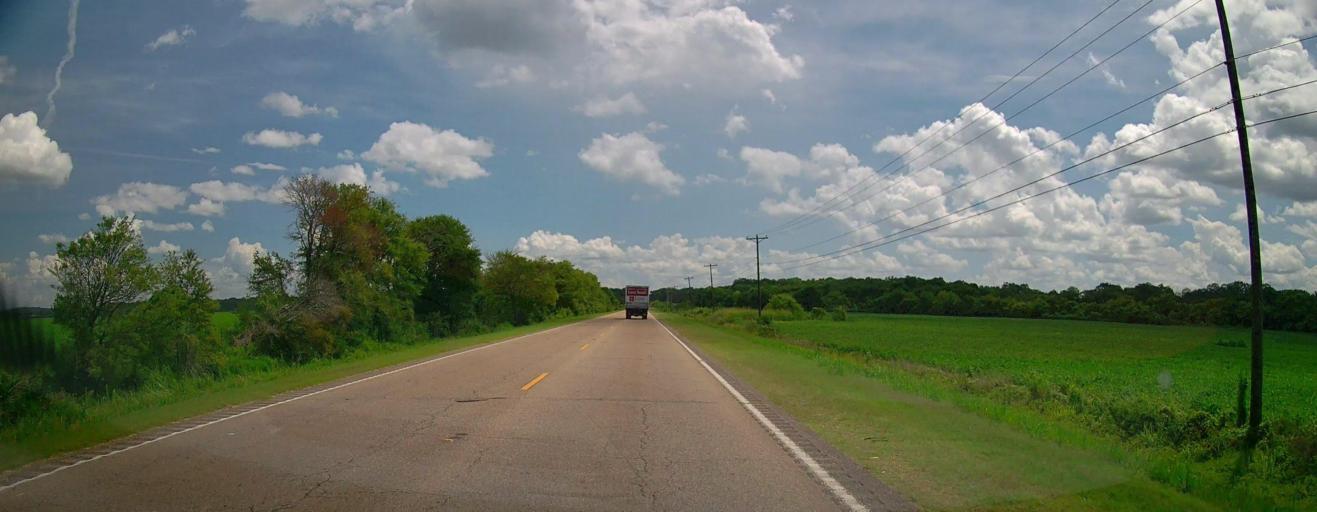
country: US
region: Mississippi
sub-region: Lee County
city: Shannon
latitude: 34.1448
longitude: -88.7194
